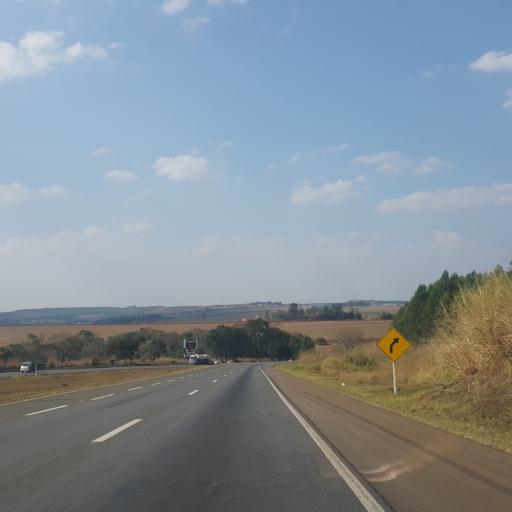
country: BR
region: Goias
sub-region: Abadiania
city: Abadiania
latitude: -16.2802
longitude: -48.7909
